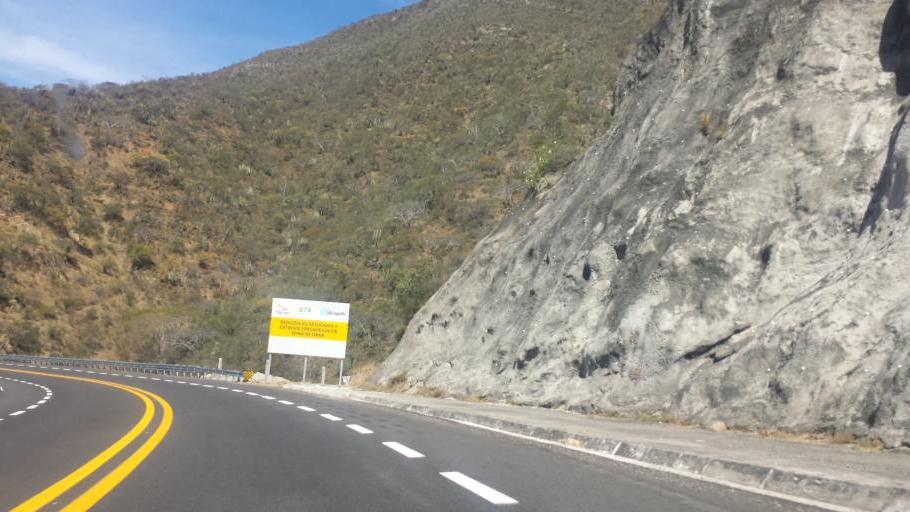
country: MX
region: Puebla
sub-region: San Jose Miahuatlan
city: San Pedro Tetitlan
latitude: 18.1035
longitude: -97.3355
